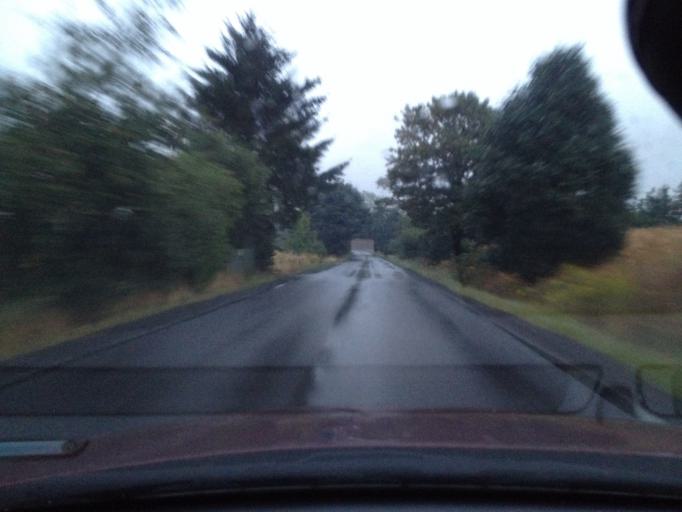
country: PL
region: Lower Silesian Voivodeship
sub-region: Powiat zgorzelecki
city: Lagow
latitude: 51.1983
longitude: 15.0721
